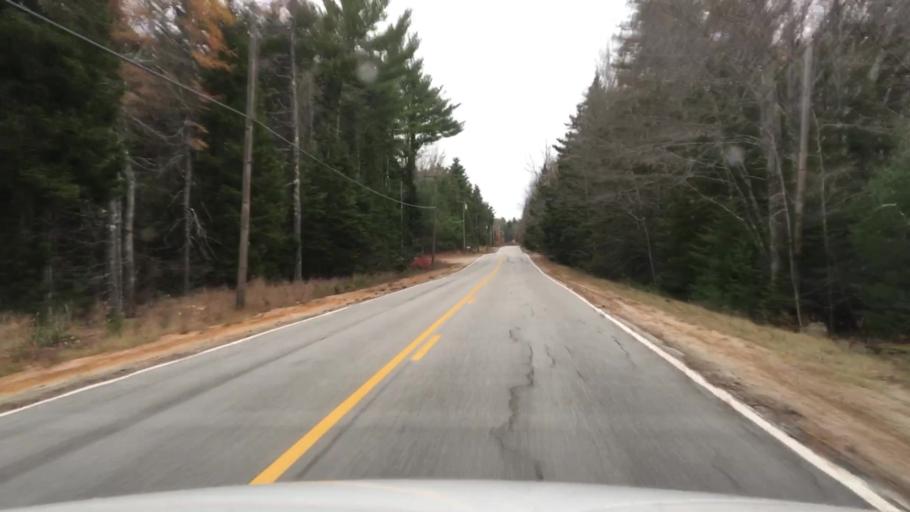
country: US
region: Maine
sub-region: Hancock County
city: Sedgwick
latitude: 44.2833
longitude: -68.5544
